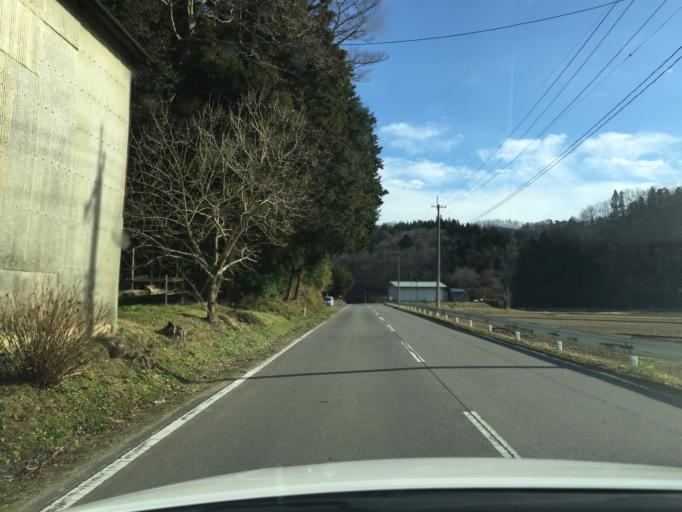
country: JP
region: Fukushima
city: Funehikimachi-funehiki
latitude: 37.2776
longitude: 140.6079
